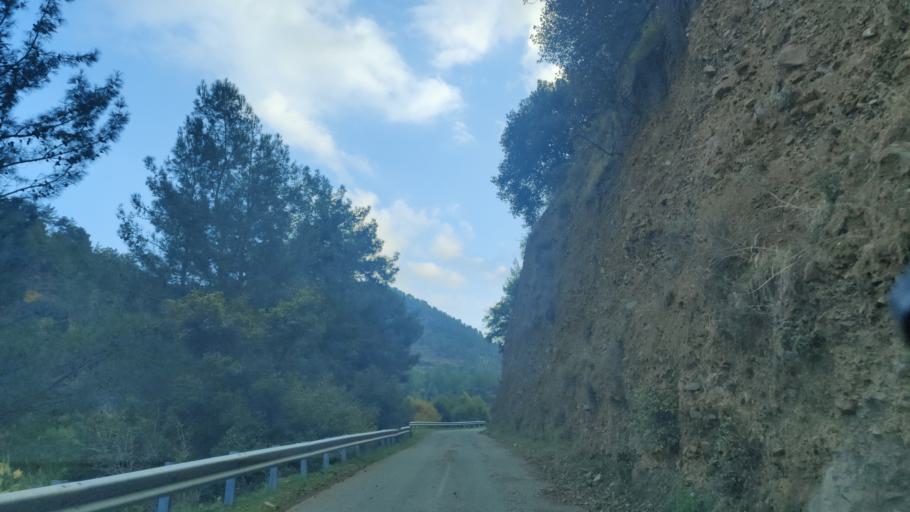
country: CY
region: Lefkosia
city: Lefka
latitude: 35.0555
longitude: 32.7349
